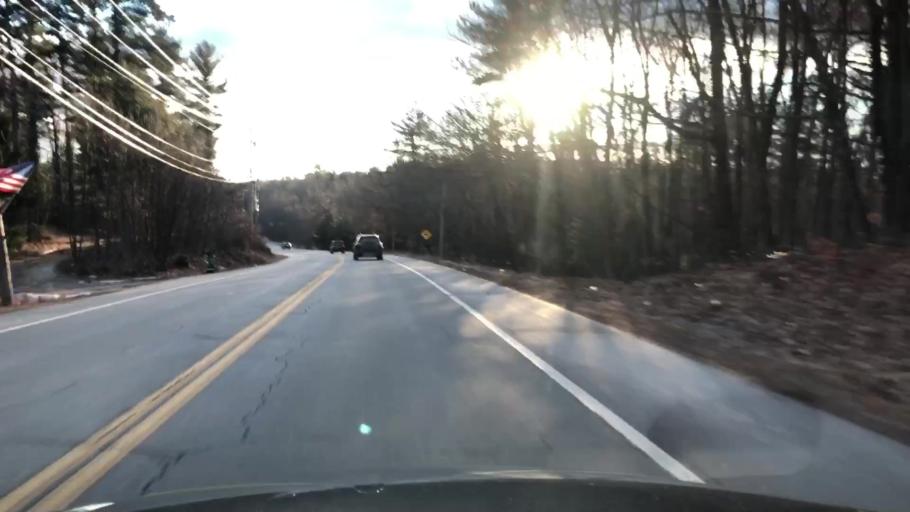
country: US
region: New Hampshire
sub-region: Hillsborough County
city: Brookline
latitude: 42.7779
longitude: -71.6664
